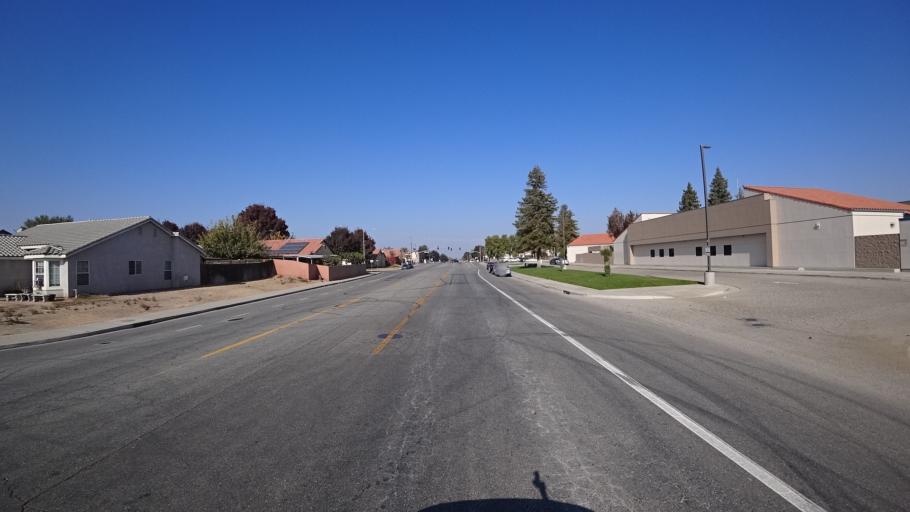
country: US
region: California
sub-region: Kern County
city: Greenfield
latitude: 35.2871
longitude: -119.0119
